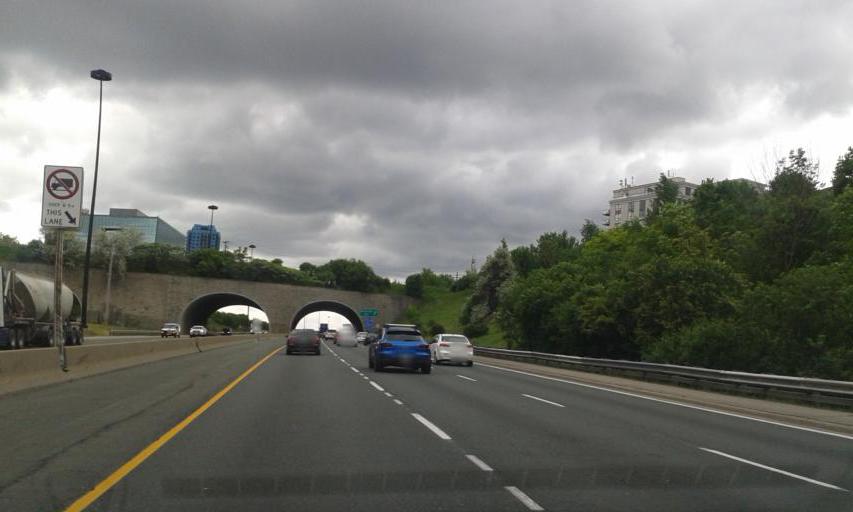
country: CA
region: Ontario
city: Willowdale
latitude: 43.7326
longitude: -79.3312
